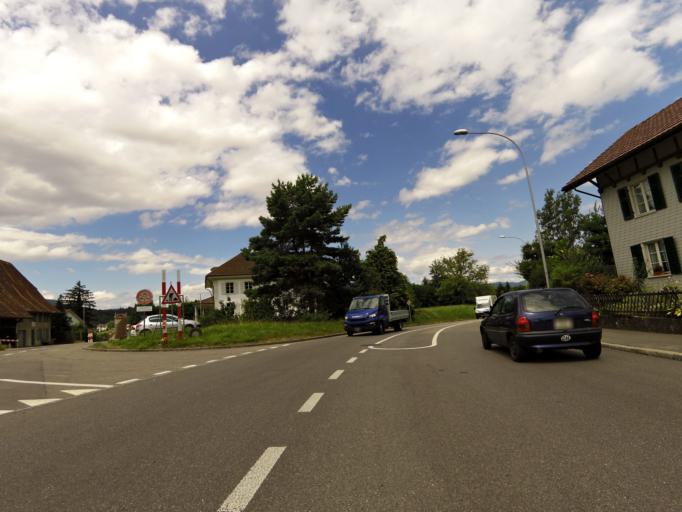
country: CH
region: Bern
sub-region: Oberaargau
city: Aarwangen
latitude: 47.2432
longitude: 7.7664
